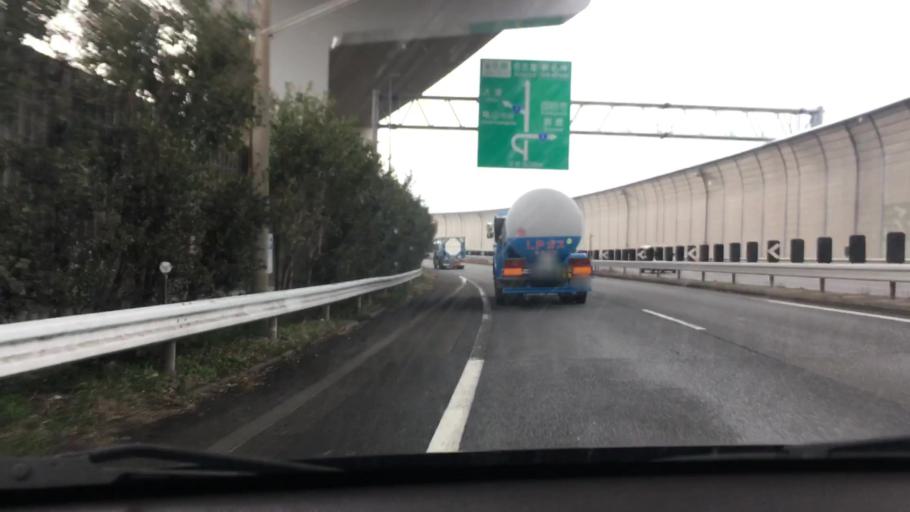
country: JP
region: Mie
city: Kameyama
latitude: 34.8508
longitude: 136.4169
